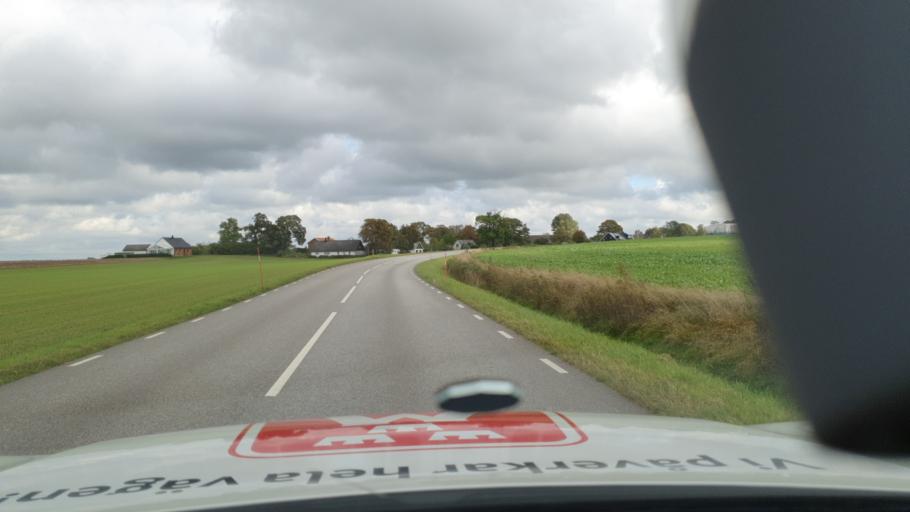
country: SE
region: Skane
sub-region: Malmo
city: Oxie
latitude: 55.4968
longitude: 13.1518
